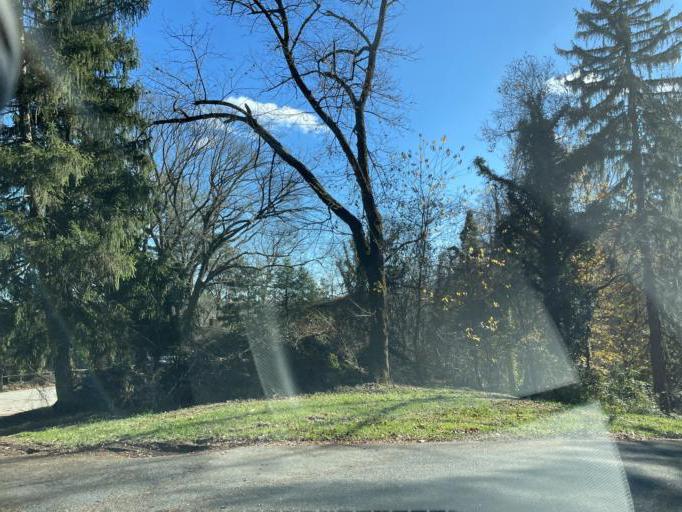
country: US
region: Maryland
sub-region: Baltimore County
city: Mays Chapel
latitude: 39.4025
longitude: -76.6559
